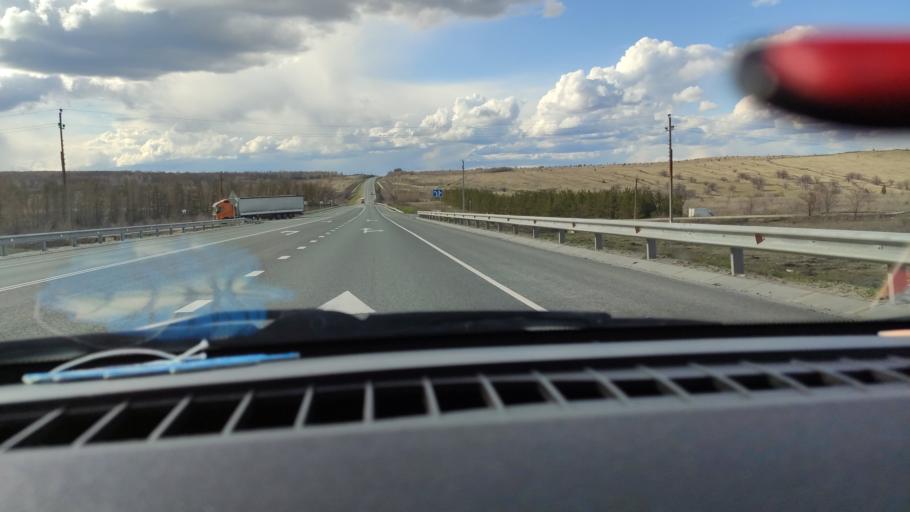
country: RU
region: Saratov
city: Shikhany
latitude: 52.1379
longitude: 47.2140
